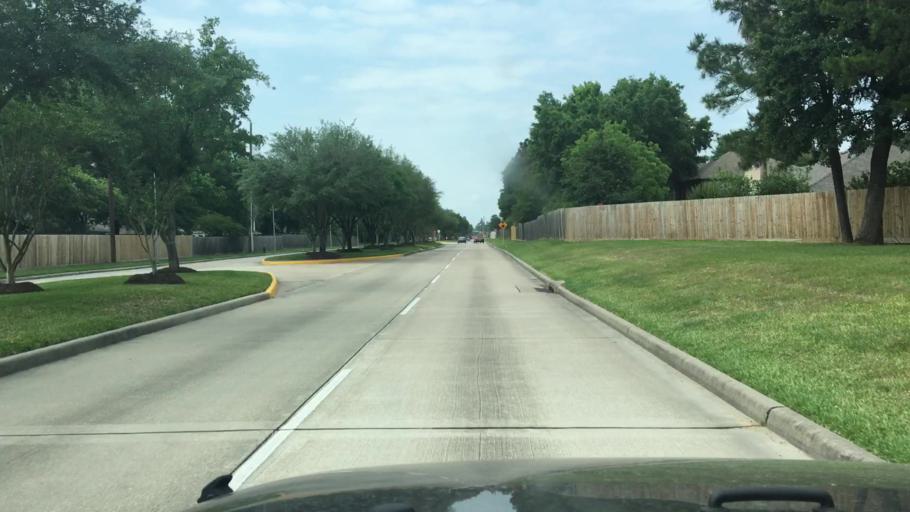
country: US
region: Texas
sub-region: Harris County
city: Atascocita
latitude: 29.9661
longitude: -95.2105
